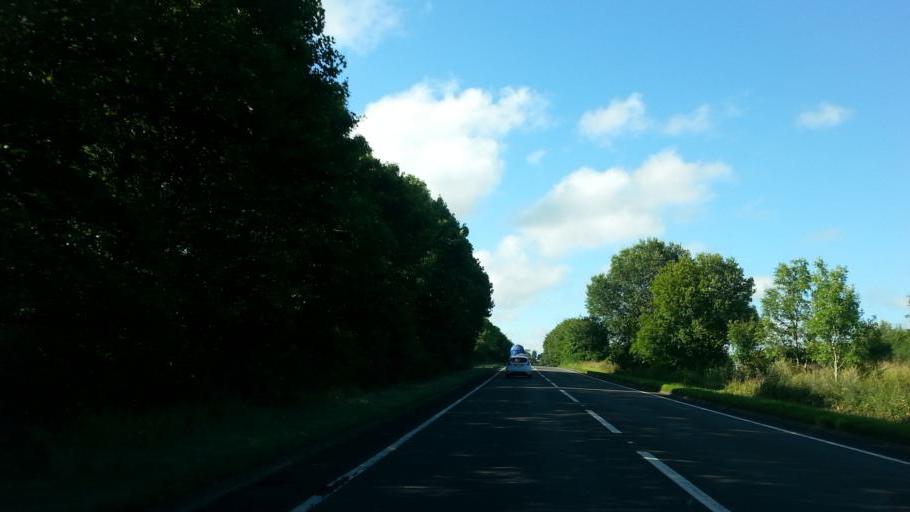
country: GB
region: England
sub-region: District of Rutland
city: South Luffenham
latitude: 52.5619
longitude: -0.5737
